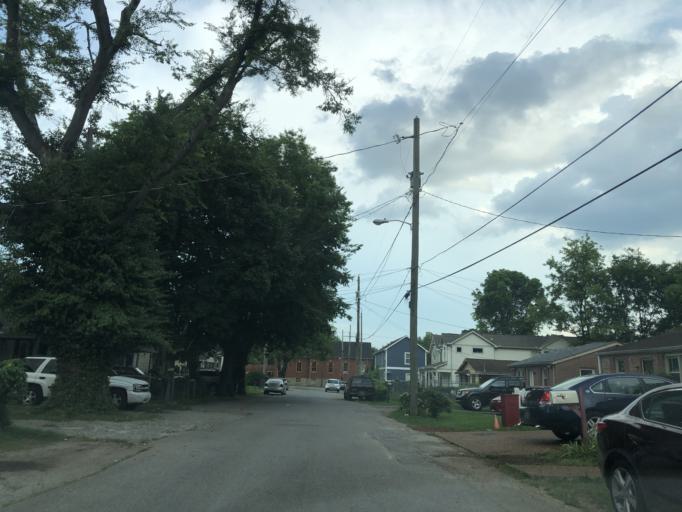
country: US
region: Tennessee
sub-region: Davidson County
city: Nashville
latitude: 36.1857
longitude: -86.8048
